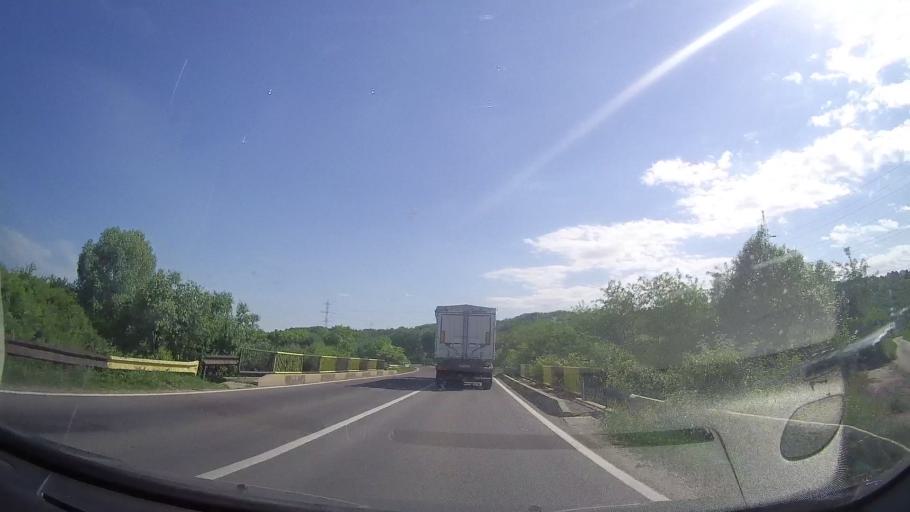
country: RO
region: Prahova
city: Drajna de Jos
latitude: 45.2288
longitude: 26.0303
